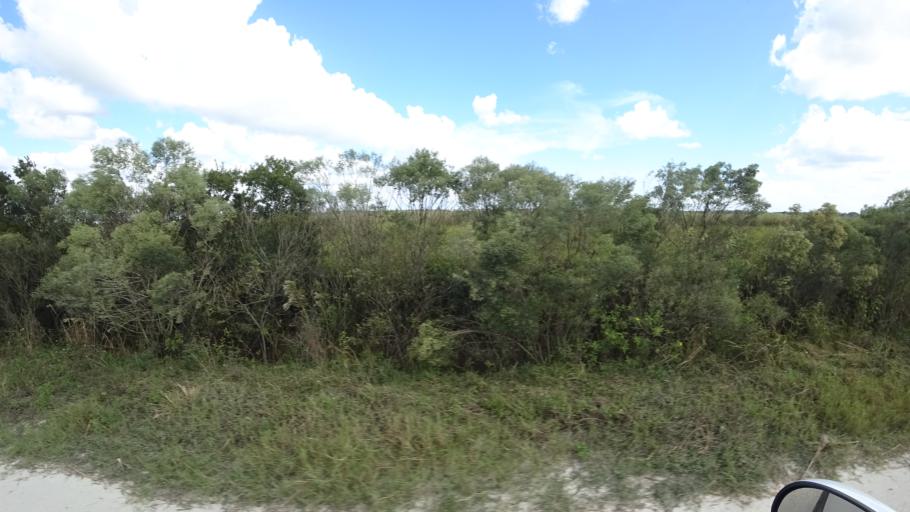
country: US
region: Florida
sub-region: DeSoto County
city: Arcadia
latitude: 27.3187
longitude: -82.1051
